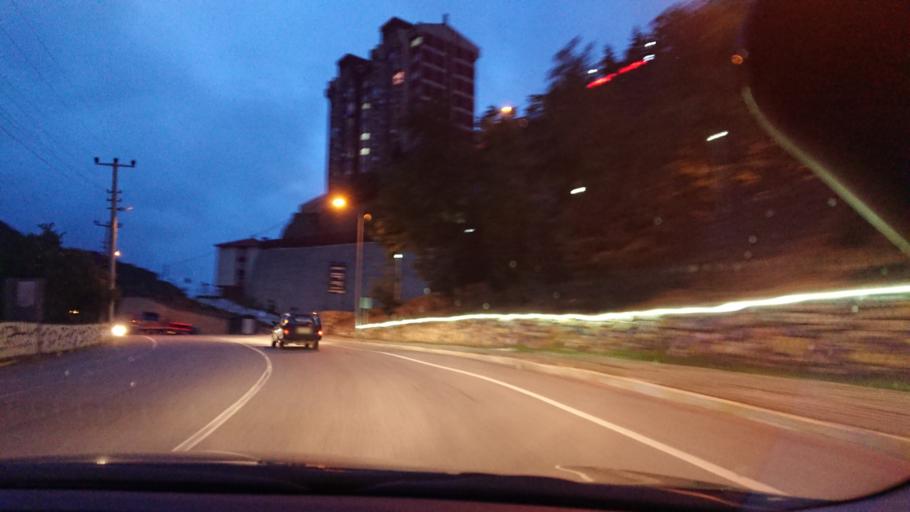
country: TR
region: Gumushane
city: Kurtun
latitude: 40.6715
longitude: 39.1401
